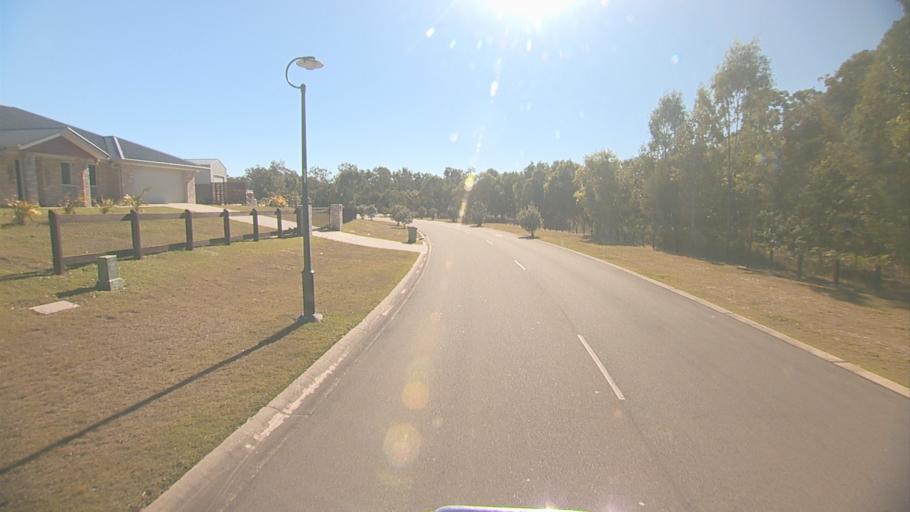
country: AU
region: Queensland
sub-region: Logan
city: North Maclean
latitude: -27.7539
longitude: 152.9662
